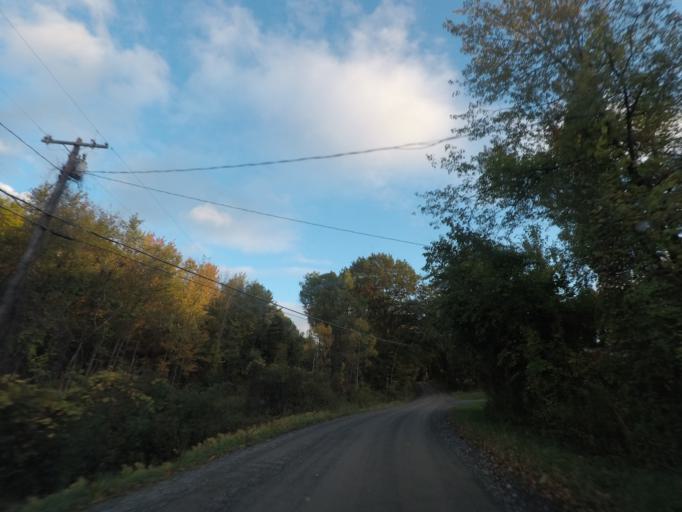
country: US
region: New York
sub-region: Rensselaer County
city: Nassau
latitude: 42.5158
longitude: -73.5919
